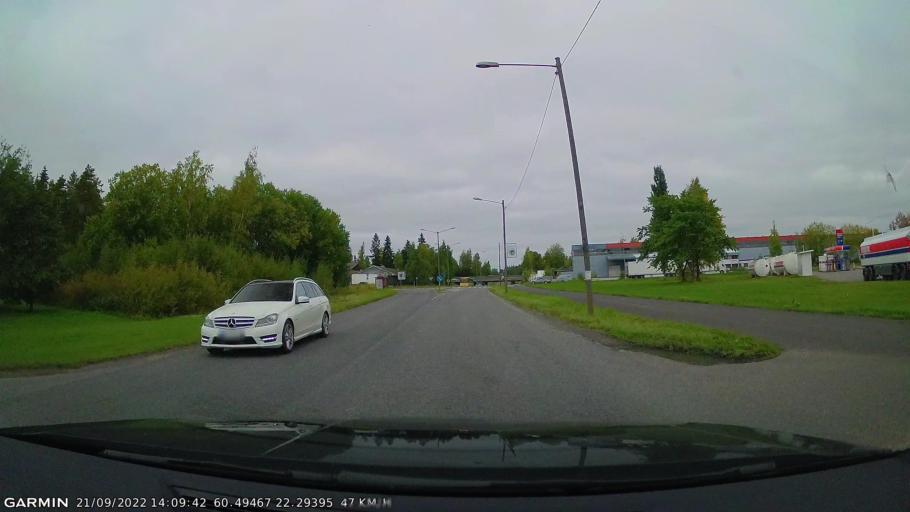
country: FI
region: Varsinais-Suomi
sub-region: Turku
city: Turku
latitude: 60.4948
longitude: 22.2940
